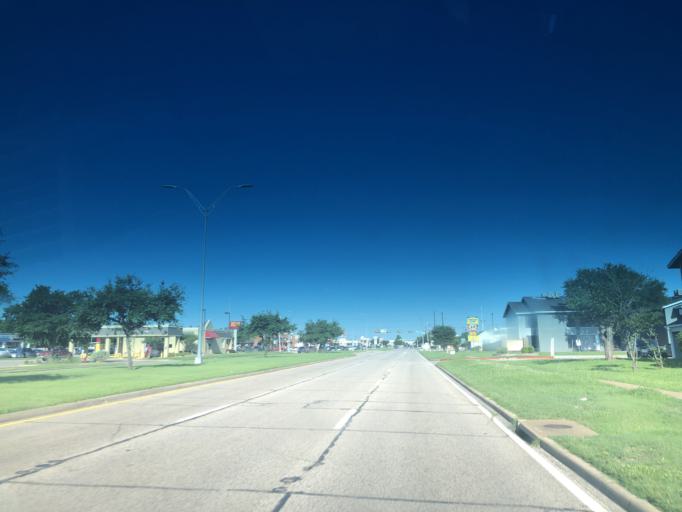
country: US
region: Texas
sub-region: Dallas County
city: Grand Prairie
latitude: 32.7097
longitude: -97.0107
